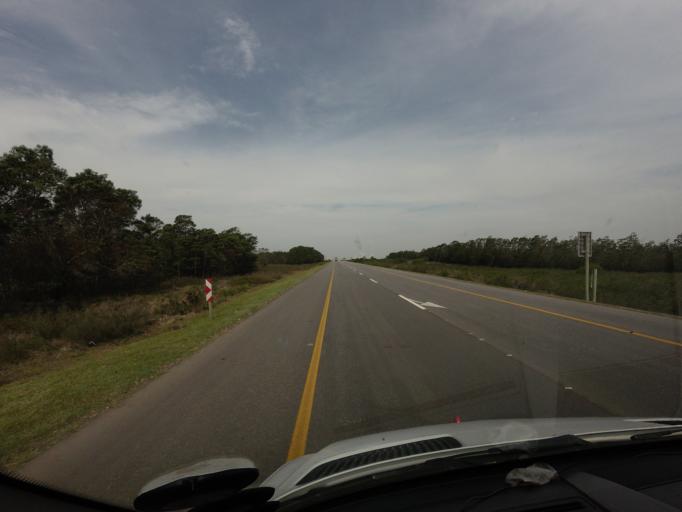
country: ZA
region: Eastern Cape
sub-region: Cacadu District Municipality
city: Kruisfontein
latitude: -34.0089
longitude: 24.7873
